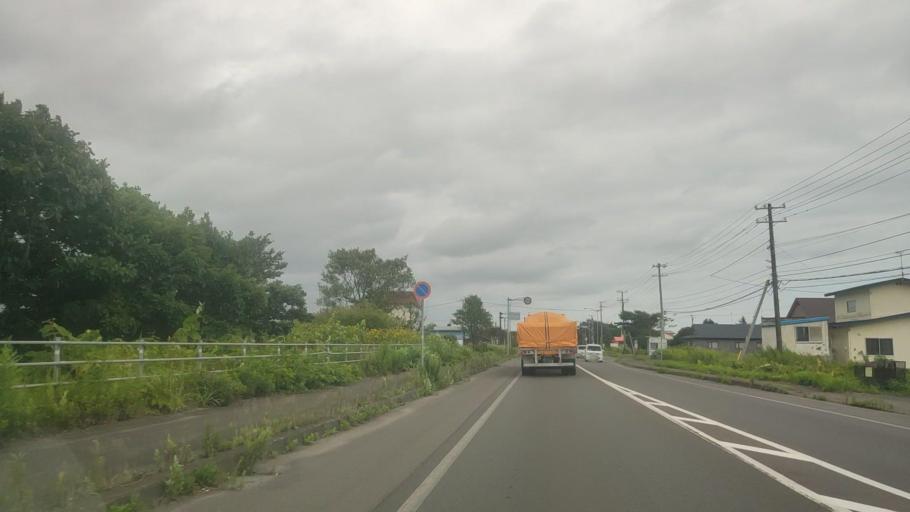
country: JP
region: Hokkaido
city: Shiraoi
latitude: 42.5233
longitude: 141.3130
